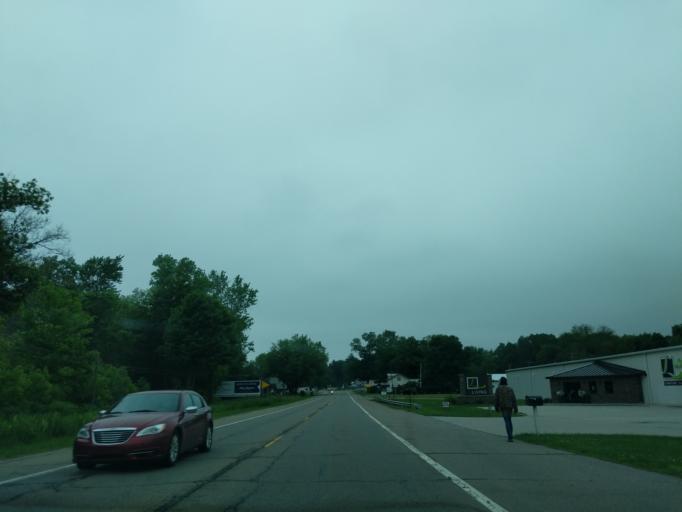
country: US
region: Michigan
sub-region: Branch County
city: Quincy
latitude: 41.9403
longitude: -84.9369
